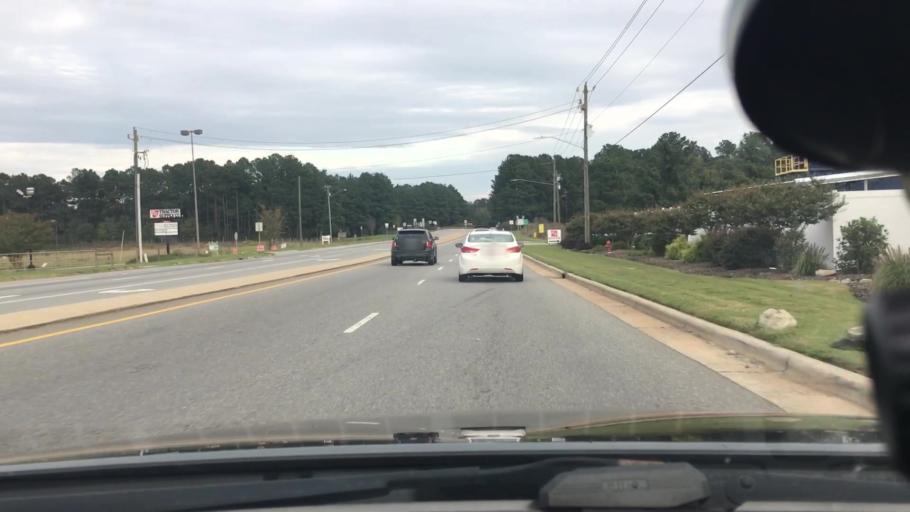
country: US
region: North Carolina
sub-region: Montgomery County
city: Biscoe
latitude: 35.3606
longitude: -79.7694
